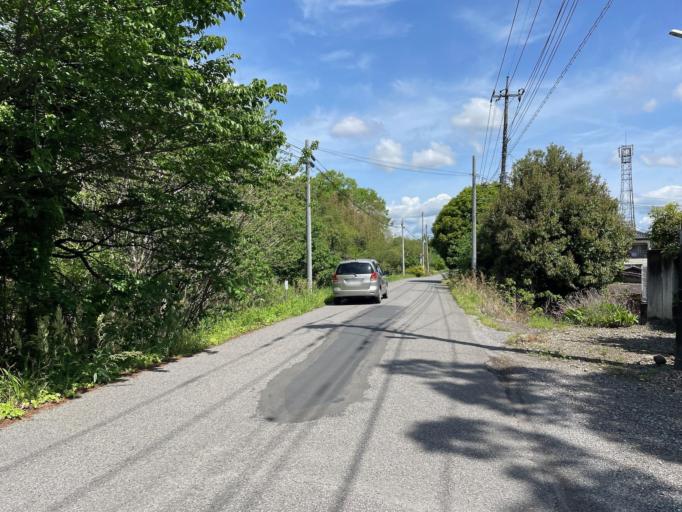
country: JP
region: Tochigi
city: Sano
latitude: 36.3143
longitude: 139.5432
